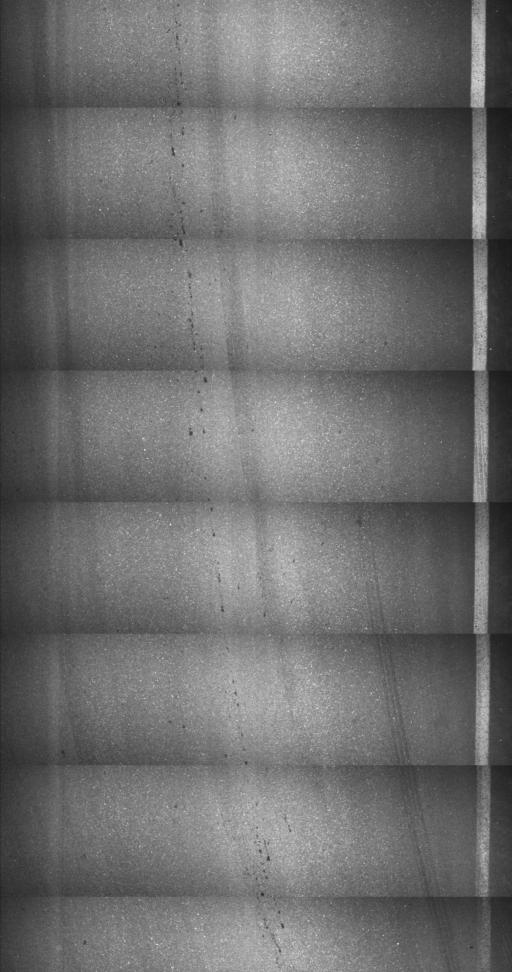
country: US
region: Vermont
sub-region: Caledonia County
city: Lyndonville
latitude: 44.8013
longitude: -71.9154
